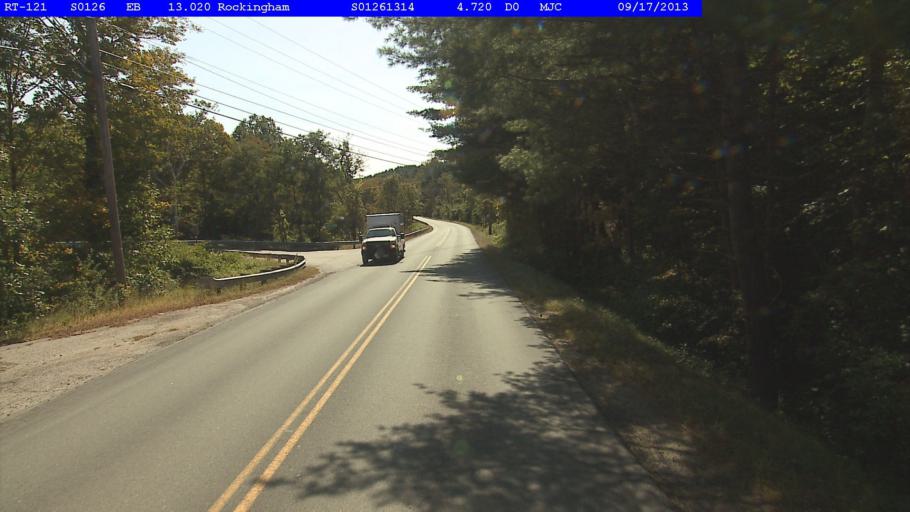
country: US
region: Vermont
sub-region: Windham County
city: Bellows Falls
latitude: 43.1316
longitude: -72.4819
